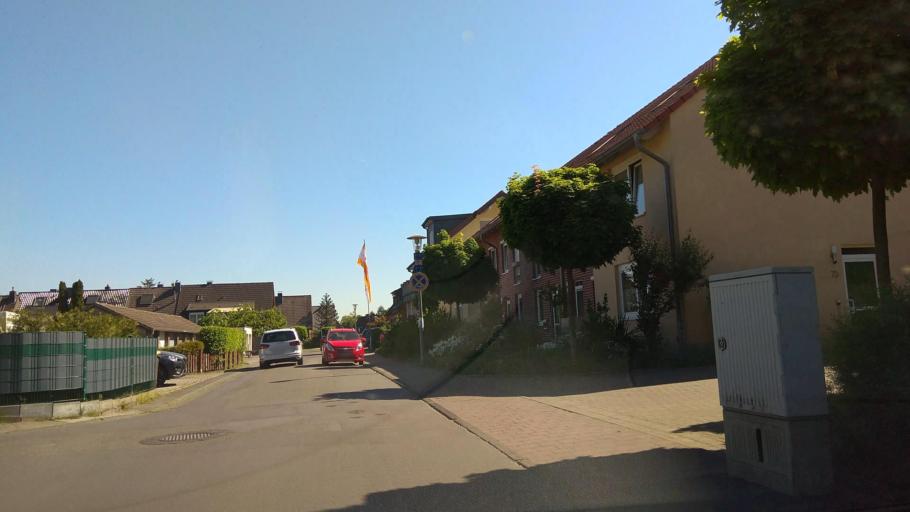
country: DE
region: North Rhine-Westphalia
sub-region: Regierungsbezirk Munster
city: Gladbeck
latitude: 51.5637
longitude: 6.9593
